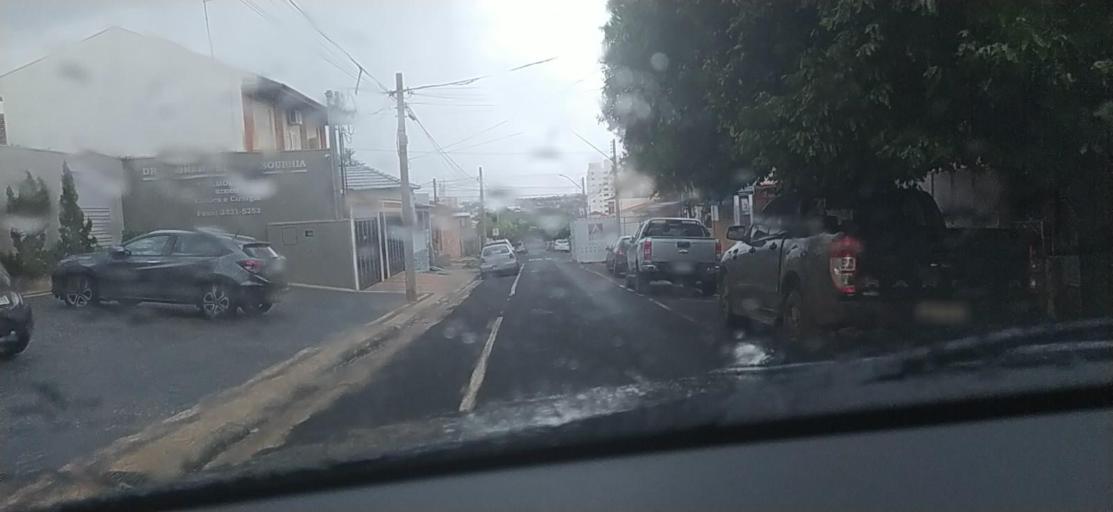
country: BR
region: Sao Paulo
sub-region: Catanduva
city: Catanduva
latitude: -21.1388
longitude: -48.9777
